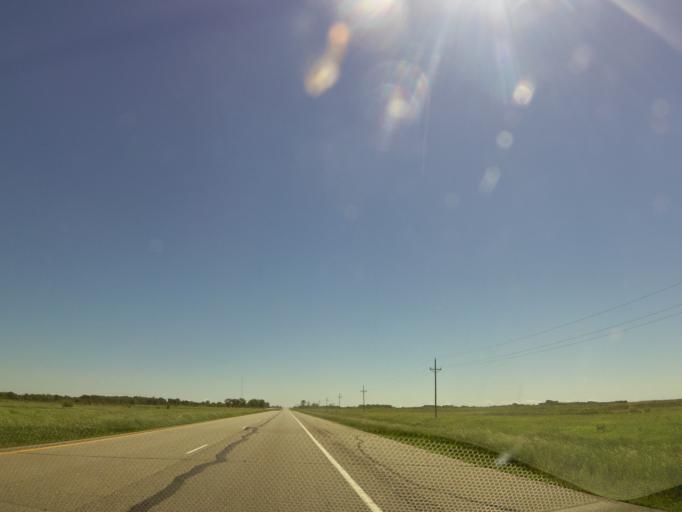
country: US
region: Minnesota
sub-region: Red Lake County
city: Red Lake Falls
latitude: 47.7604
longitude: -96.3679
